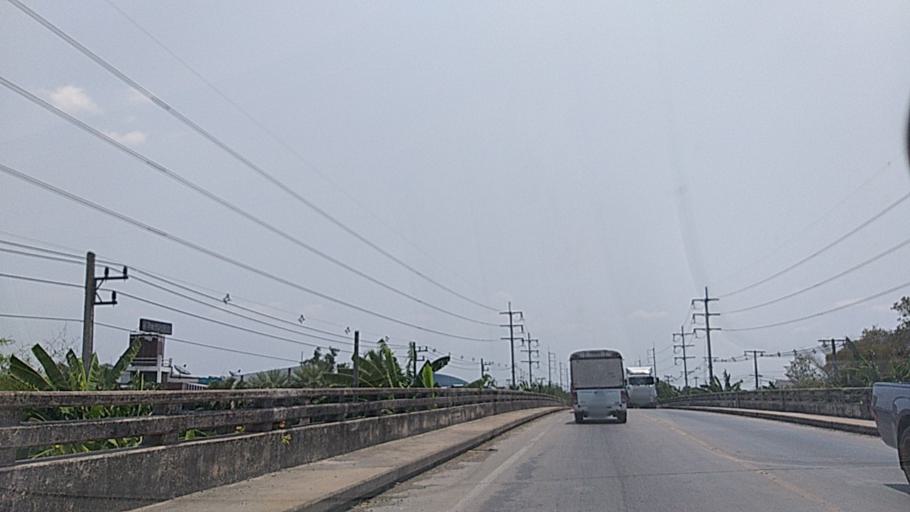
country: TH
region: Chachoengsao
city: Bang Nam Priao
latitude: 13.8440
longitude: 101.0523
